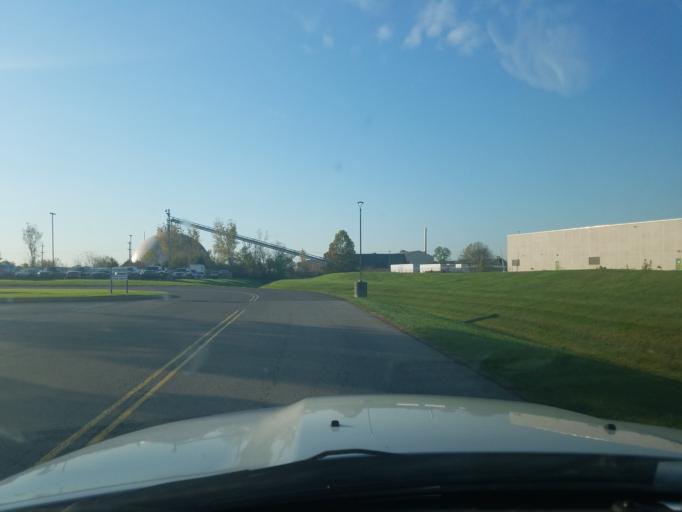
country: US
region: Indiana
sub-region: Jackson County
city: Seymour
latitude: 38.9666
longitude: -85.8618
